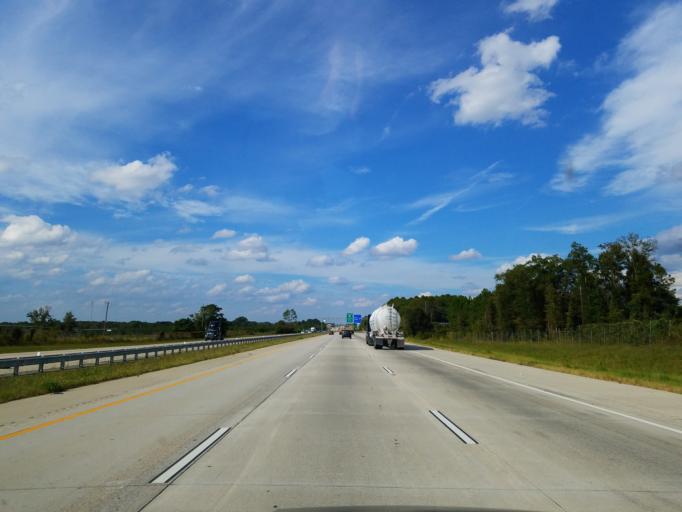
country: US
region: Georgia
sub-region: Dooly County
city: Vienna
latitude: 32.0681
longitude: -83.7633
